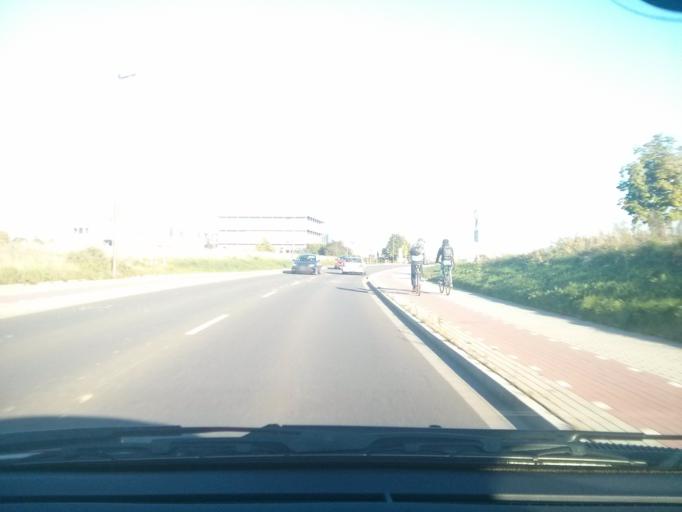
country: DE
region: North Rhine-Westphalia
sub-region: Regierungsbezirk Arnsberg
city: Dortmund
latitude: 51.4952
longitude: 7.4218
